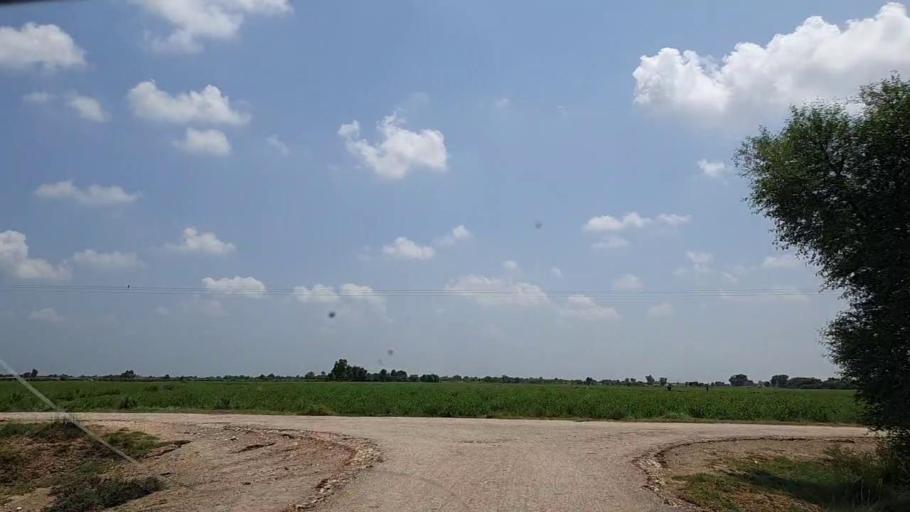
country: PK
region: Sindh
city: Tharu Shah
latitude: 27.0026
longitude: 68.0595
